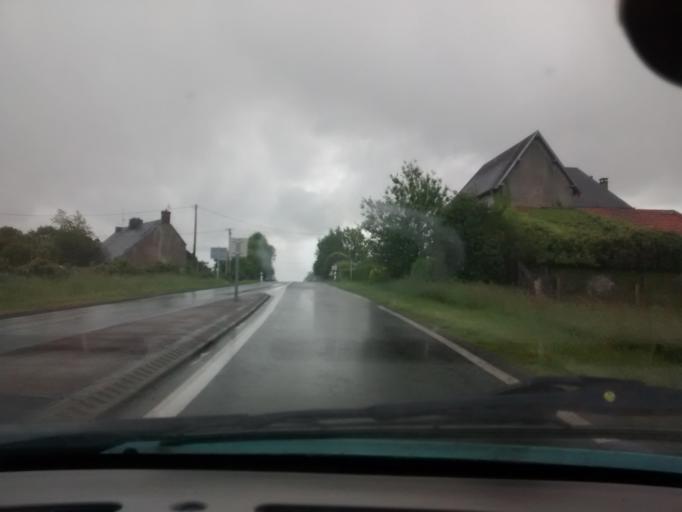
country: FR
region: Lower Normandy
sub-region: Departement de la Manche
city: Conde-sur-Vire
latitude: 49.0790
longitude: -1.0287
